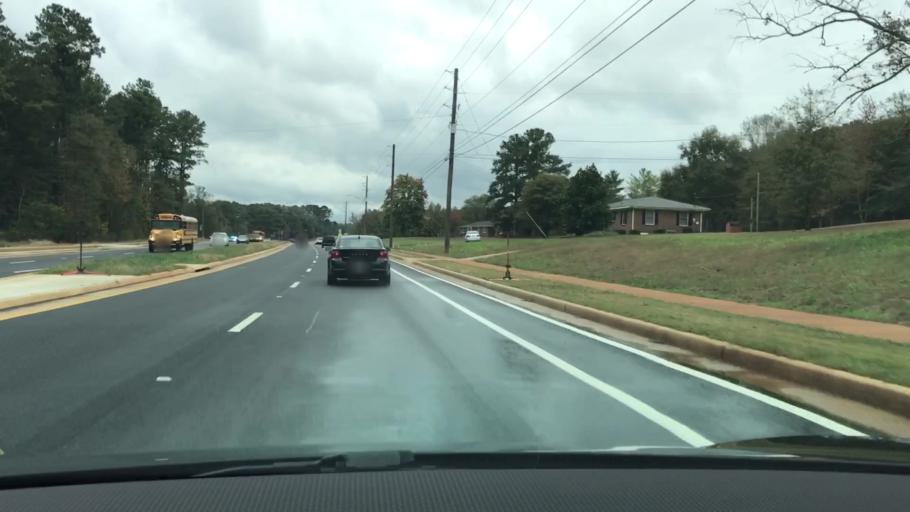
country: US
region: Georgia
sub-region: Oconee County
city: Watkinsville
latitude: 33.8939
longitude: -83.4601
